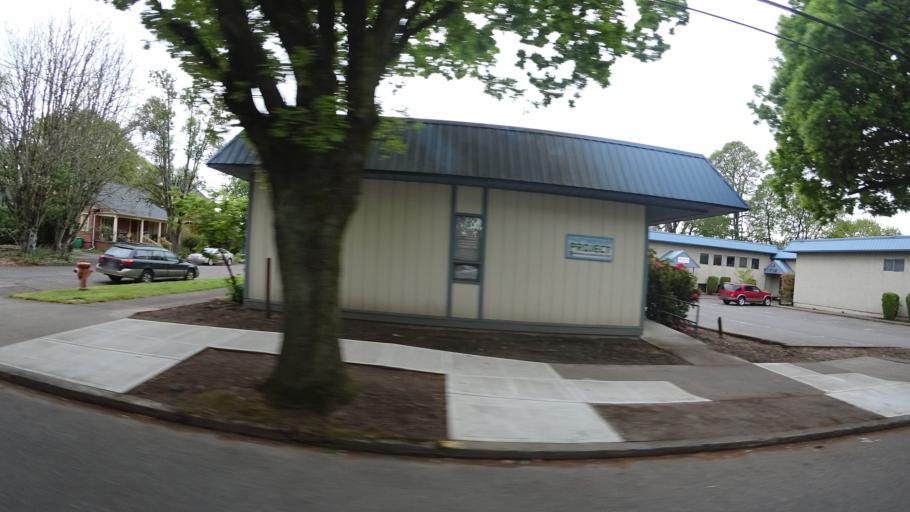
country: US
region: Oregon
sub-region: Clackamas County
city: Milwaukie
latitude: 45.4826
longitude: -122.6497
